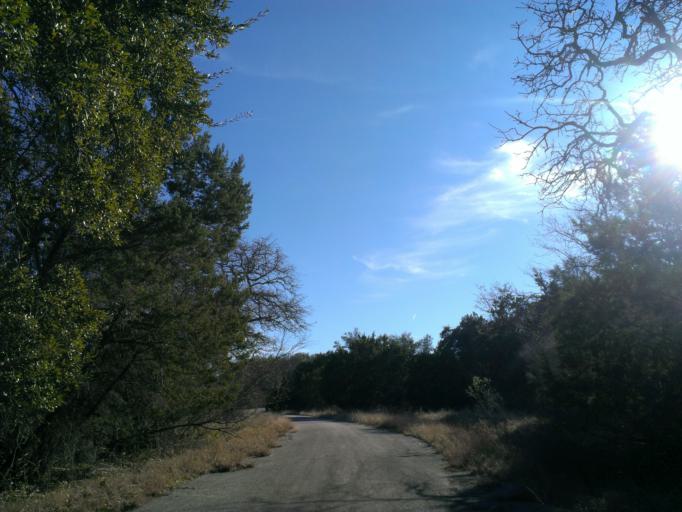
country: US
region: Texas
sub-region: Llano County
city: Horseshoe Bay
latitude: 30.5392
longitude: -98.3368
